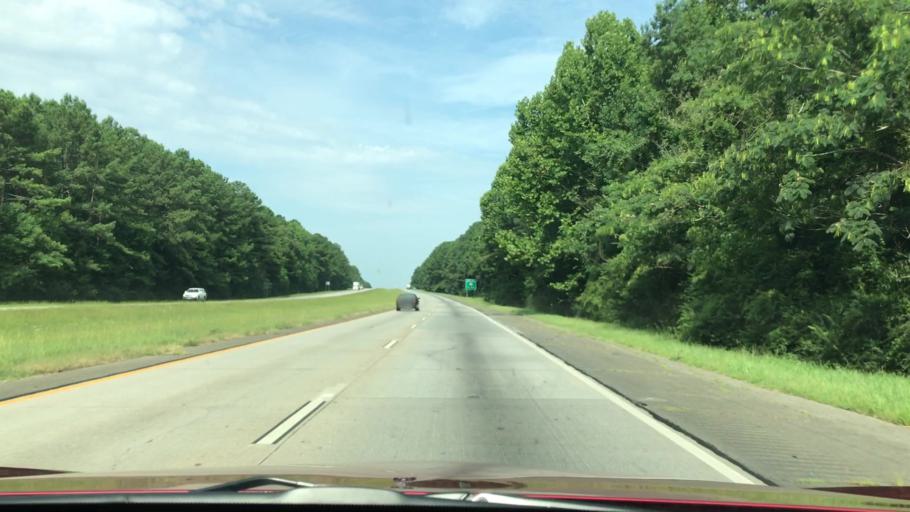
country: US
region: Georgia
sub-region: Taliaferro County
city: Crawfordville
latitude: 33.5004
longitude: -82.7930
